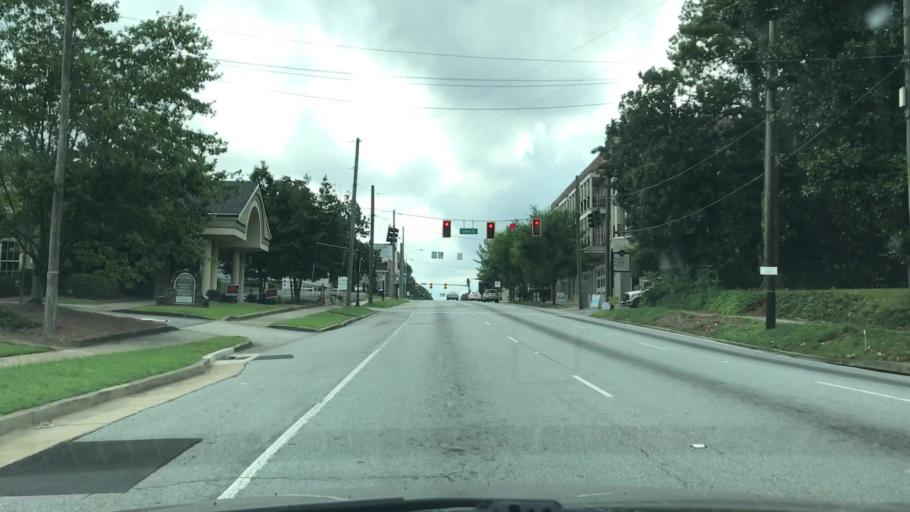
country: US
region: Georgia
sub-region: Gwinnett County
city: Lawrenceville
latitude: 33.9561
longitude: -83.9918
